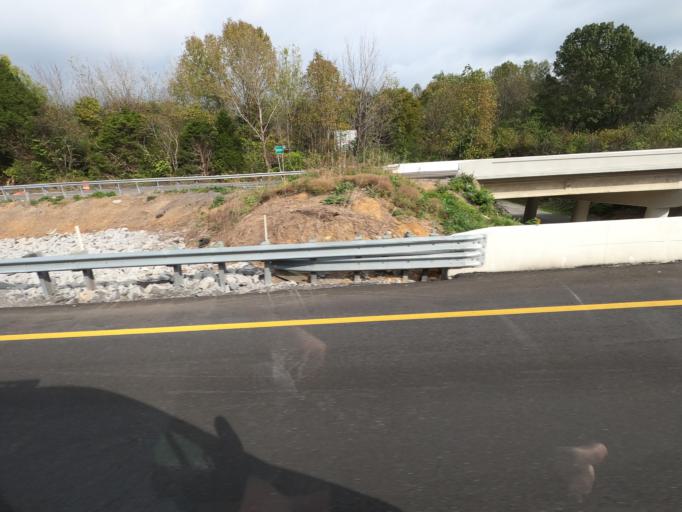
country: US
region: Tennessee
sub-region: Williamson County
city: Fairview
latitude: 36.0235
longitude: -87.1879
